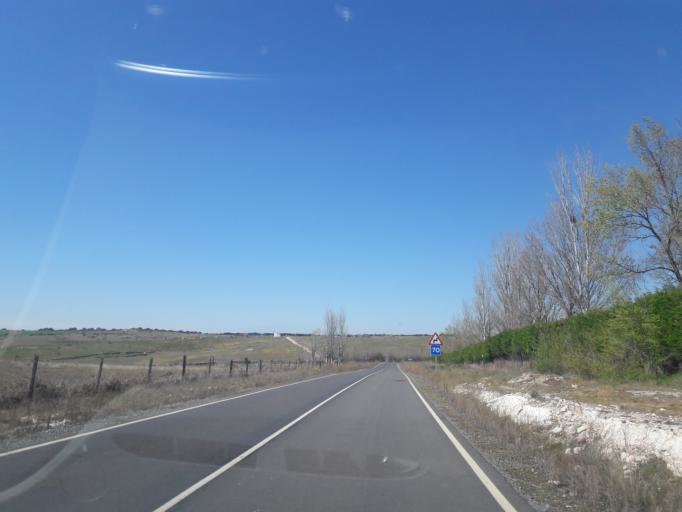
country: ES
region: Castille and Leon
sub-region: Provincia de Salamanca
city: Martinamor
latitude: 40.8070
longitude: -5.6069
